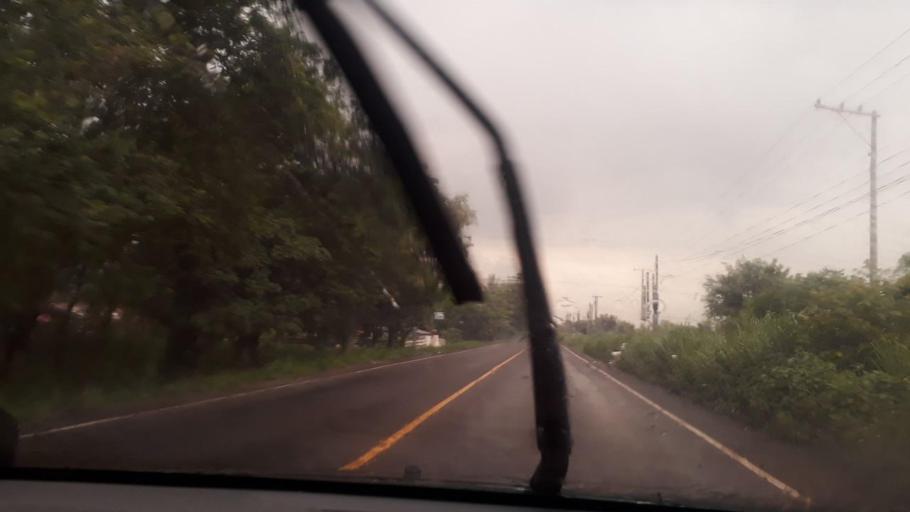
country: GT
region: Escuintla
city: Guanagazapa
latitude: 14.0987
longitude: -90.6070
